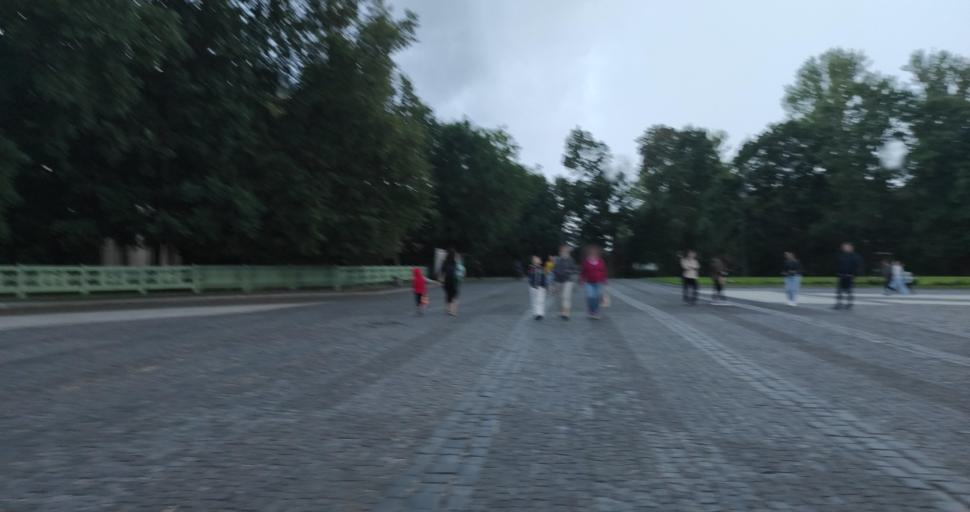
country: RU
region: St.-Petersburg
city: Kronshtadt
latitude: 59.9917
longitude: 29.7766
